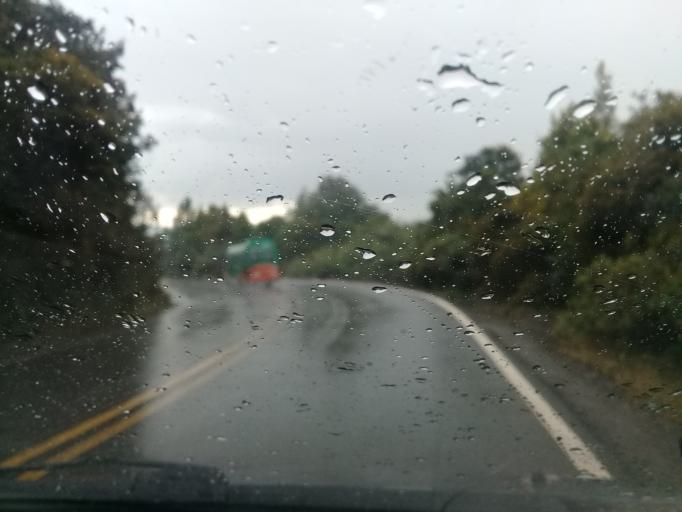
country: CO
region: Cundinamarca
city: Guasca
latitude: 4.8427
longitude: -73.8312
